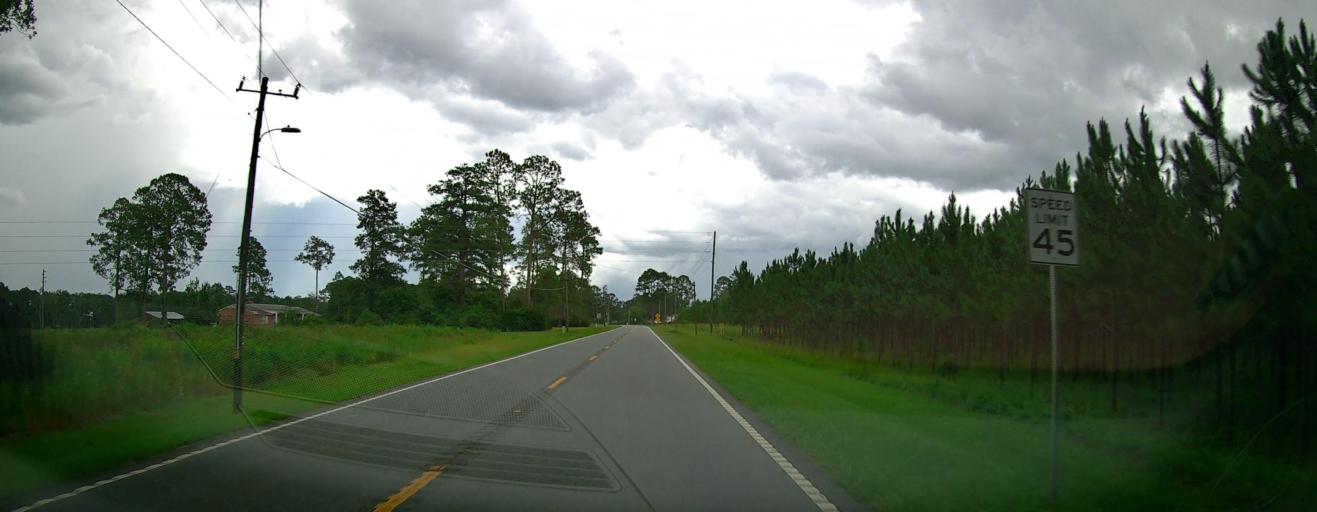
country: US
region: Georgia
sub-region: Pierce County
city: Blackshear
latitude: 31.3826
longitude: -82.1343
